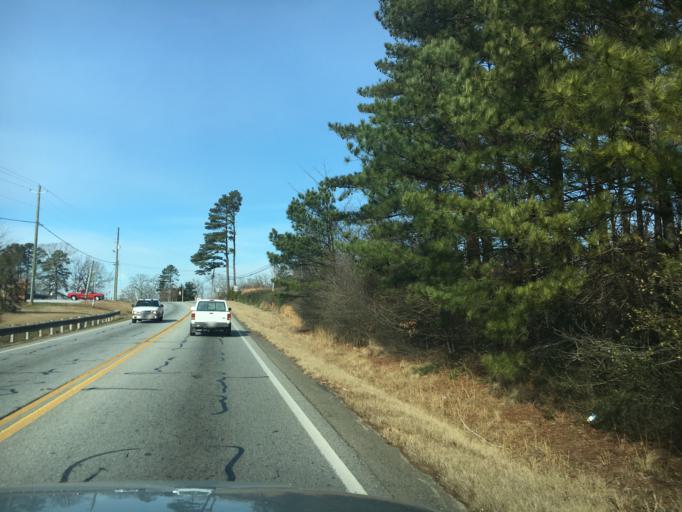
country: US
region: Georgia
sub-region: Jackson County
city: Braselton
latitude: 34.1035
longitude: -83.7618
